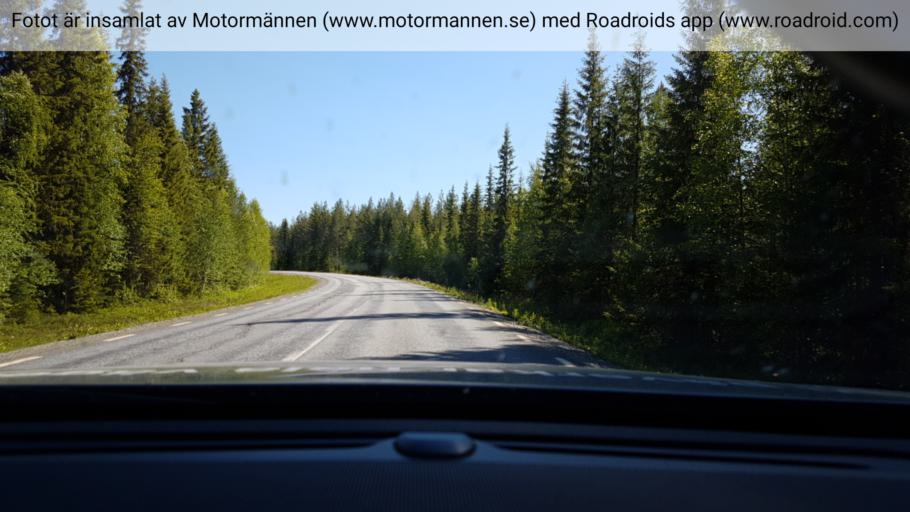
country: SE
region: Vaesterbotten
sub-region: Vilhelmina Kommun
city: Sjoberg
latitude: 64.7588
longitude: 16.1570
